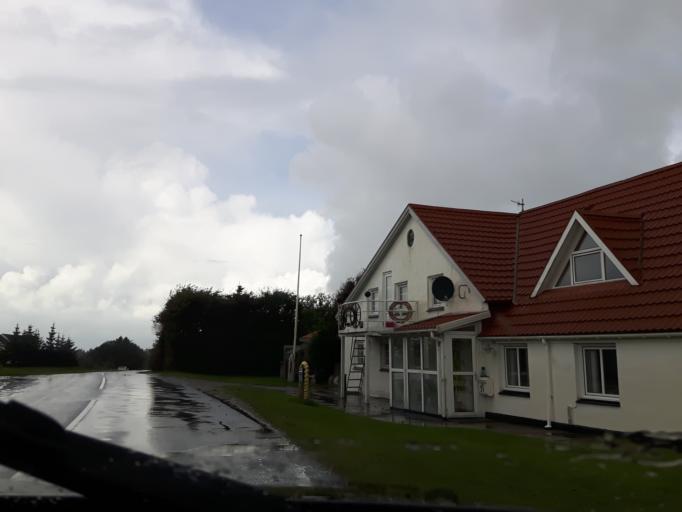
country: DK
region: North Denmark
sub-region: Thisted Kommune
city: Hanstholm
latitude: 57.1029
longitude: 8.6365
